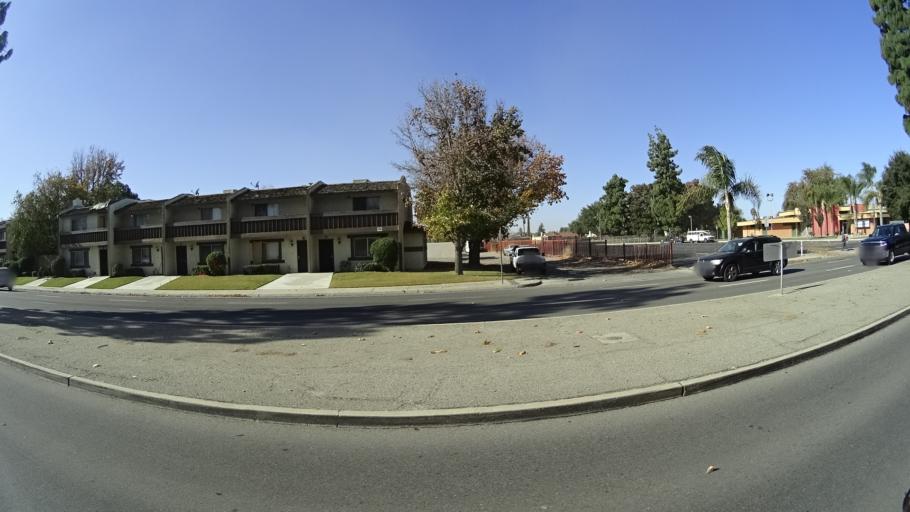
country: US
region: California
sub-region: Kern County
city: Bakersfield
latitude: 35.3277
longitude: -119.0562
